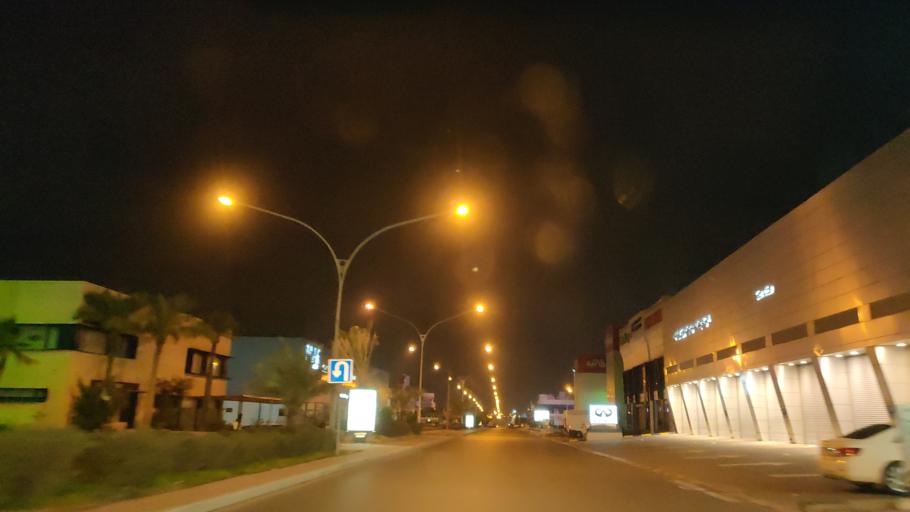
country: KW
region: Al Asimah
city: Ar Rabiyah
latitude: 29.3055
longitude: 47.9362
